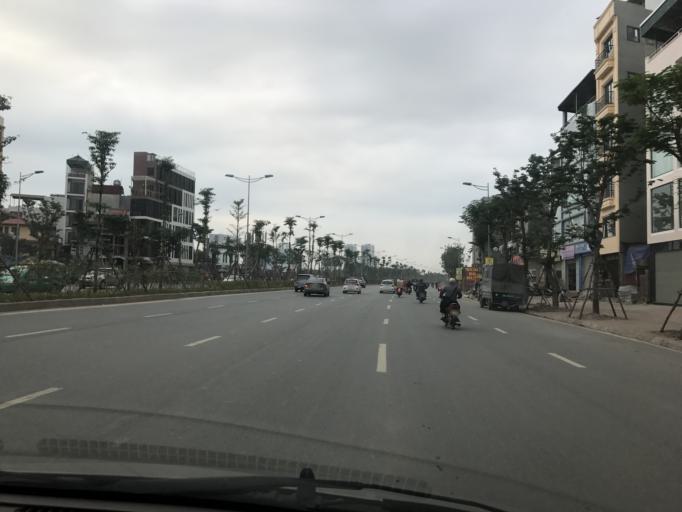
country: VN
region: Ha Noi
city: Cau Giay
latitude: 21.0499
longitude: 105.8047
